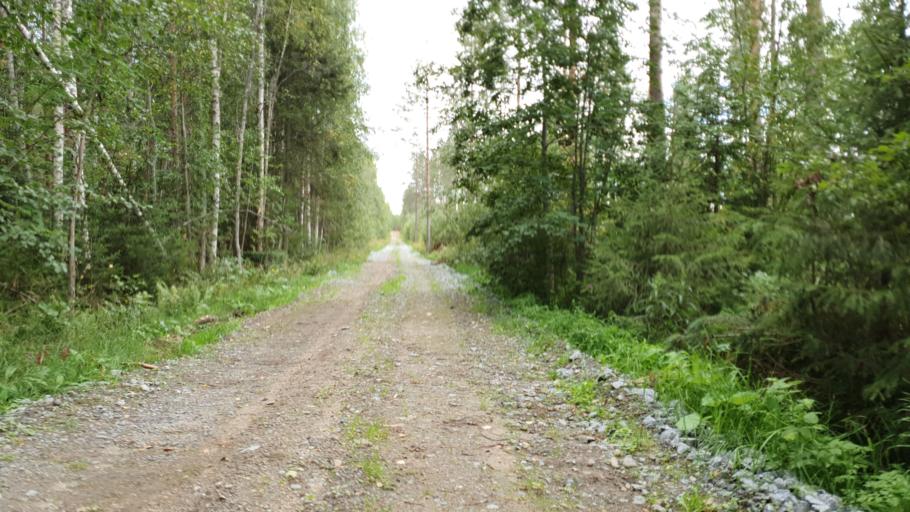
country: FI
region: Kainuu
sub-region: Kehys-Kainuu
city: Kuhmo
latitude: 64.1333
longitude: 29.4508
